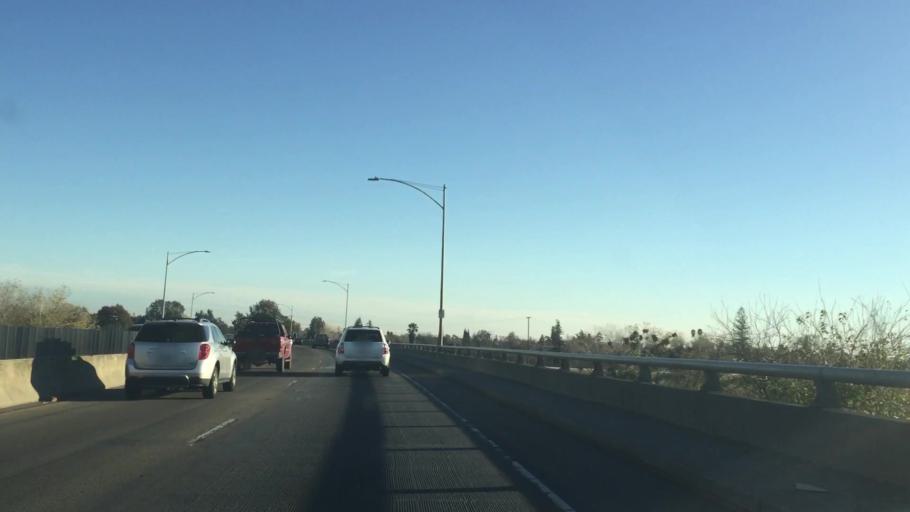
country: US
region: California
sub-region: Yuba County
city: Marysville
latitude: 39.1314
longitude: -121.5878
